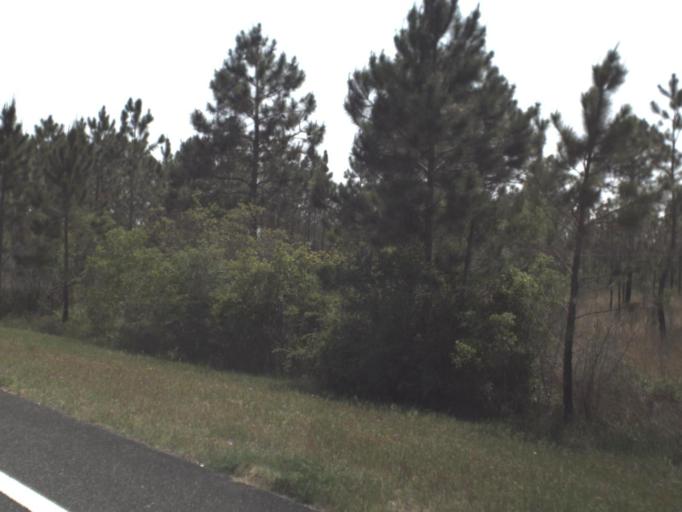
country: US
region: Florida
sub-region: Santa Rosa County
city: Tiger Point
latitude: 30.4854
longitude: -87.0797
